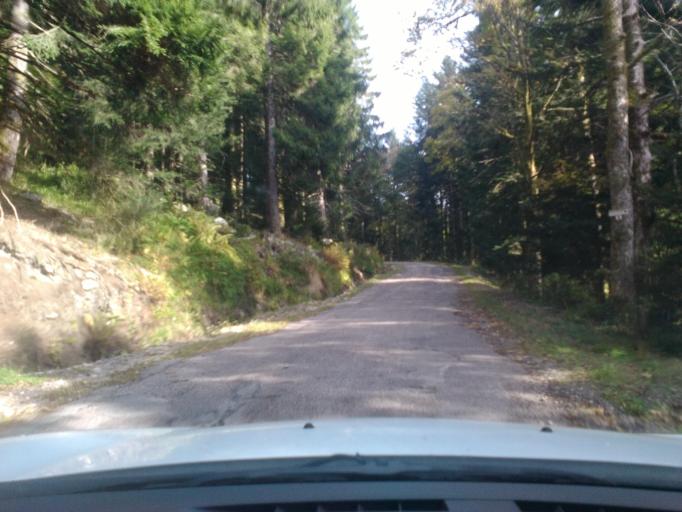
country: FR
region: Lorraine
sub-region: Departement des Vosges
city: Gerardmer
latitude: 48.0494
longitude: 6.8853
